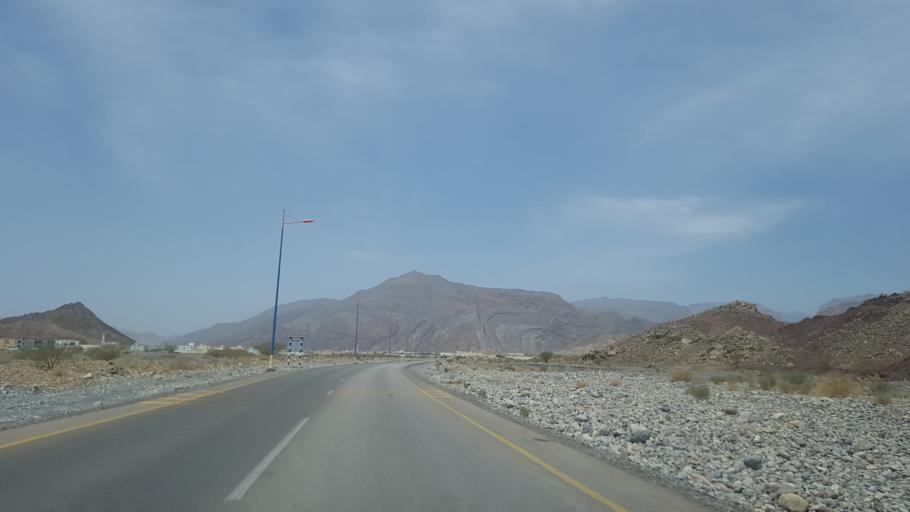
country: OM
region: Muhafazat ad Dakhiliyah
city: Izki
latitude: 22.8945
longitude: 57.6843
